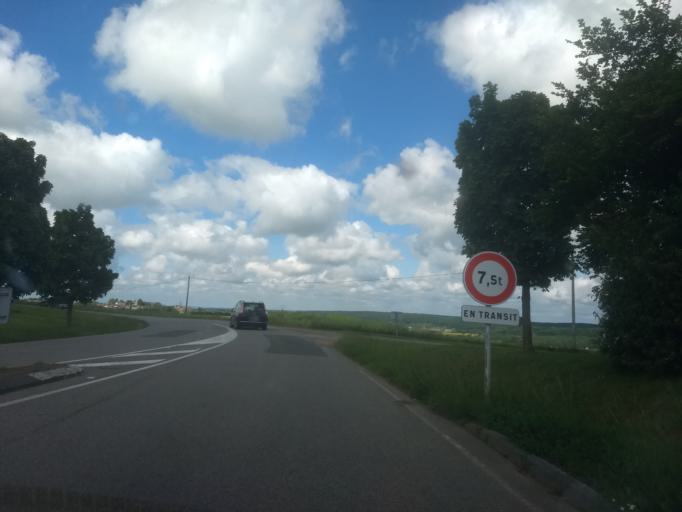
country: FR
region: Lower Normandy
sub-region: Departement de l'Orne
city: Belleme
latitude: 48.3810
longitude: 0.5849
